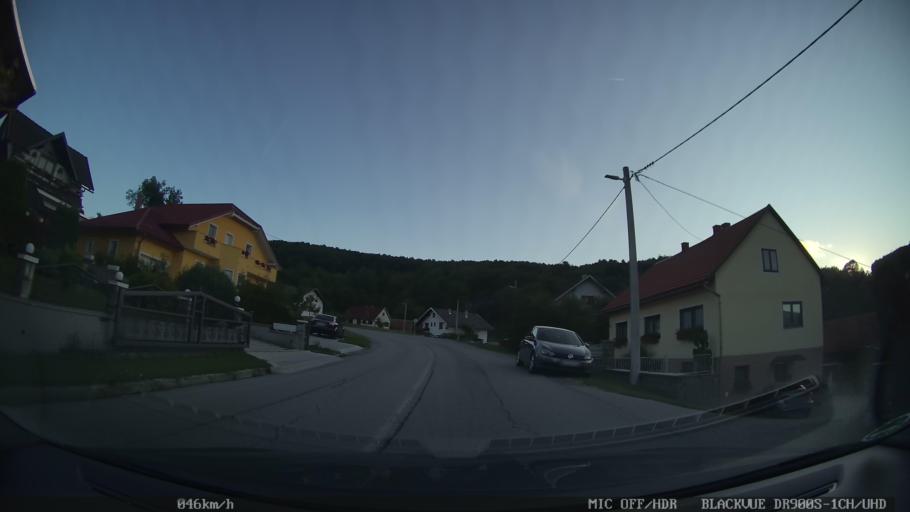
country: HR
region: Karlovacka
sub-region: Grad Ogulin
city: Ogulin
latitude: 45.2685
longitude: 15.1920
